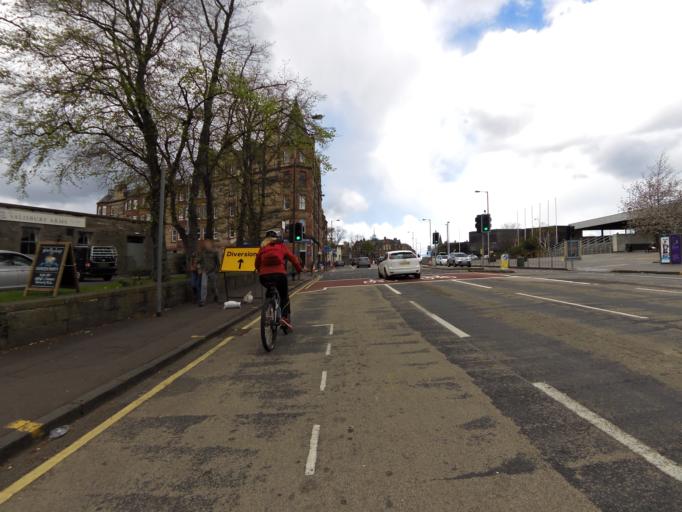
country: GB
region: Scotland
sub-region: Edinburgh
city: Edinburgh
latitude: 55.9383
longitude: -3.1734
